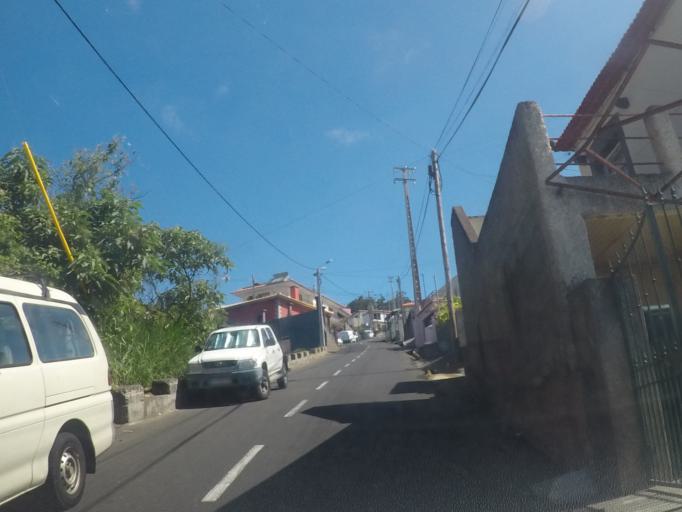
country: PT
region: Madeira
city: Camara de Lobos
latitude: 32.6727
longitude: -16.9647
